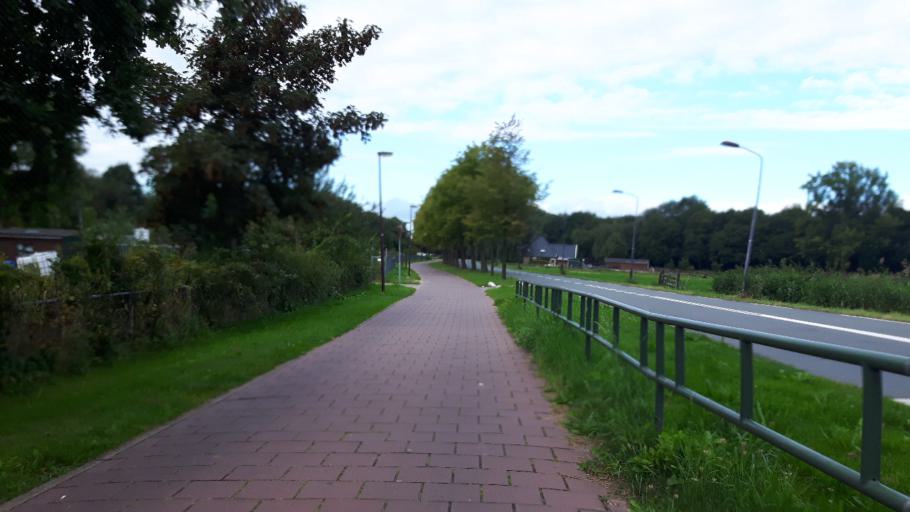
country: NL
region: North Holland
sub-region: Gemeente Hoorn
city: Hoorn
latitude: 52.6451
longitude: 5.0363
